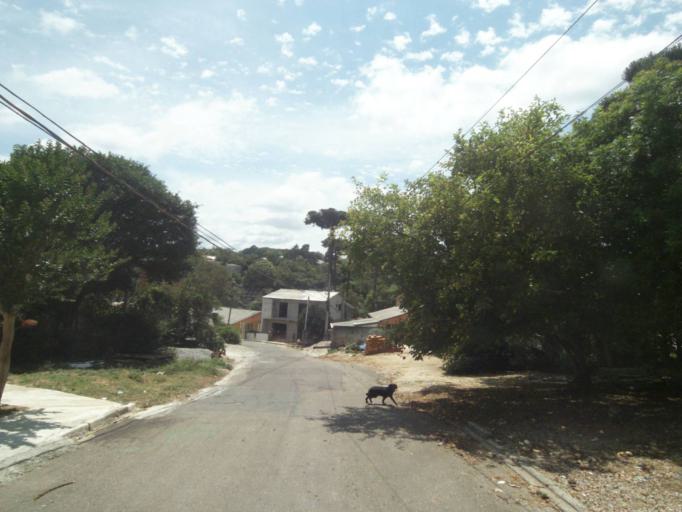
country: BR
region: Parana
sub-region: Curitiba
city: Curitiba
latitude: -25.4572
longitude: -49.3426
